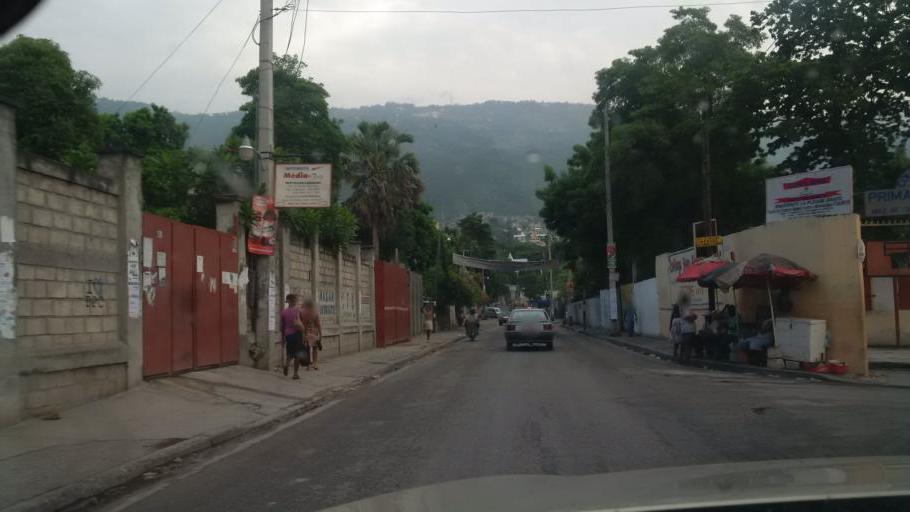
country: HT
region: Ouest
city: Port-au-Prince
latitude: 18.5355
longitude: -72.3336
